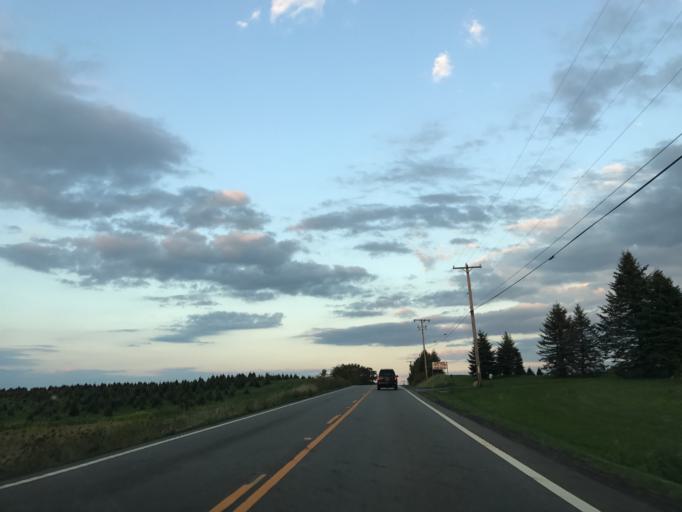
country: US
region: Ohio
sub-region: Columbiana County
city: Lisbon
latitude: 40.7700
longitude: -80.8297
